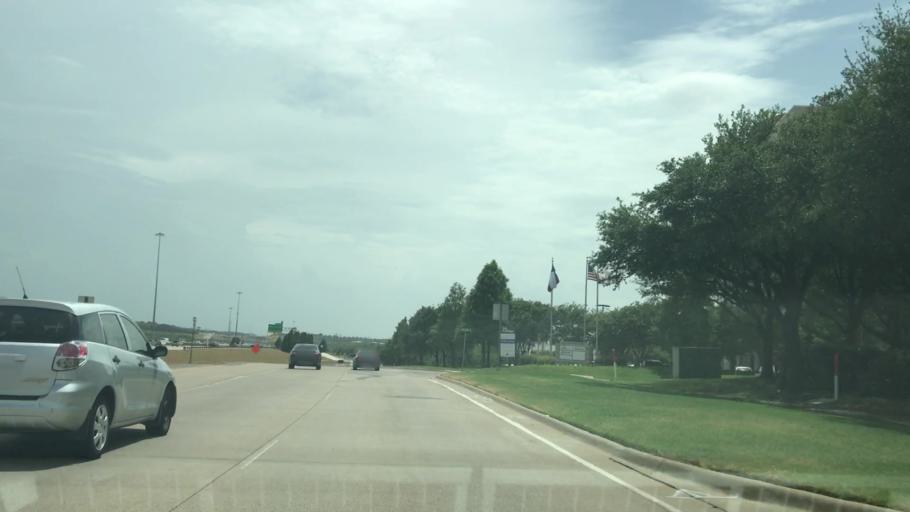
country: US
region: Texas
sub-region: Dallas County
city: Coppell
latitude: 32.8931
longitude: -96.9782
